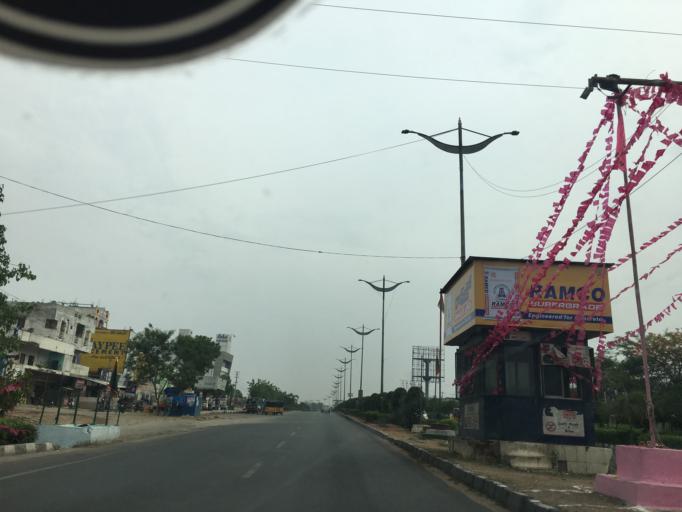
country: IN
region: Telangana
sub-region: Rangareddi
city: Balapur
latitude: 17.2978
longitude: 78.4187
